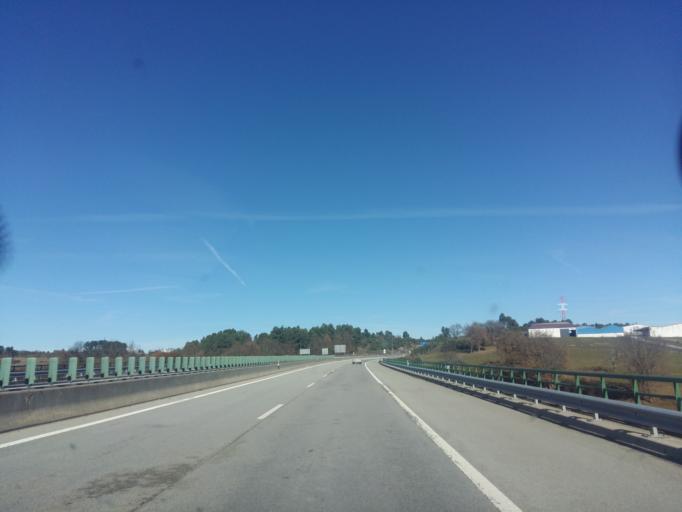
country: PT
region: Guarda
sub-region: Guarda
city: Sequeira
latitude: 40.5172
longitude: -7.2319
